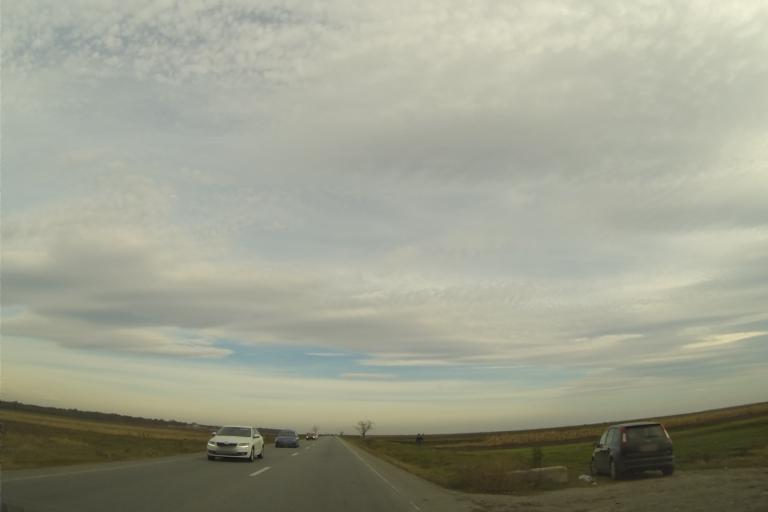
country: RO
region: Olt
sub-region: Comuna Priseaca
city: Priseaca
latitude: 44.5014
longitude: 24.4673
